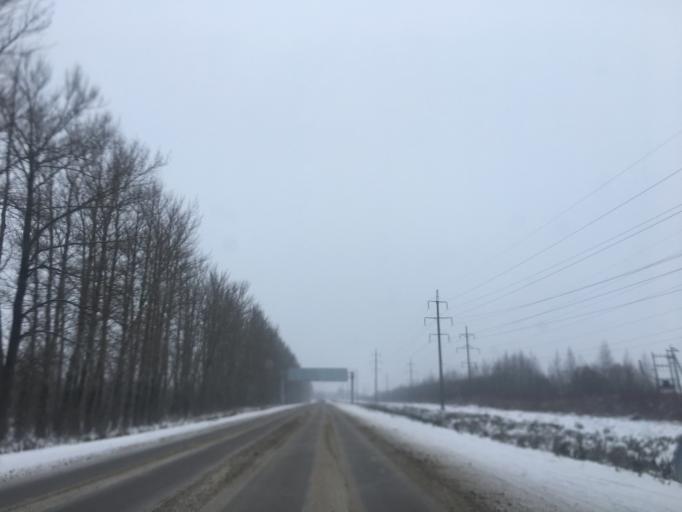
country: RU
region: Tula
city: Kosaya Gora
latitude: 54.1834
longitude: 37.5141
